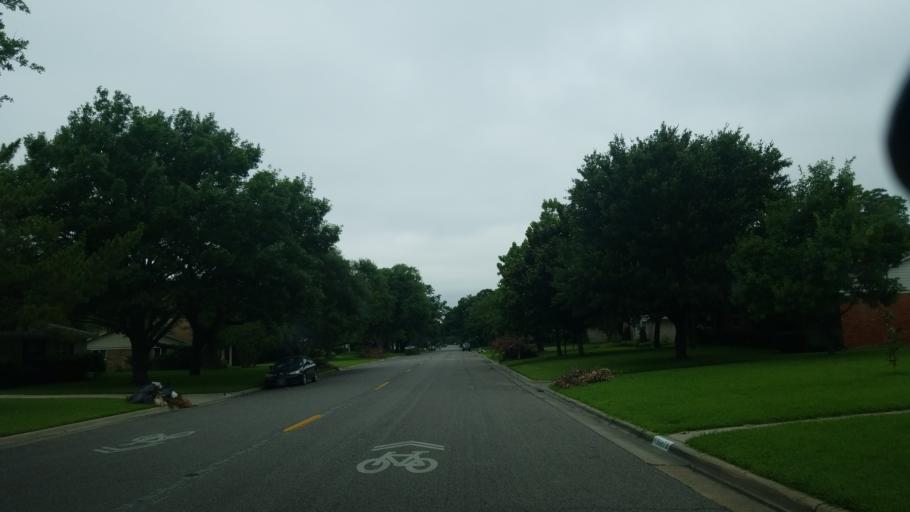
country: US
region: Texas
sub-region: Dallas County
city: Farmers Branch
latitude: 32.9023
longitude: -96.8570
